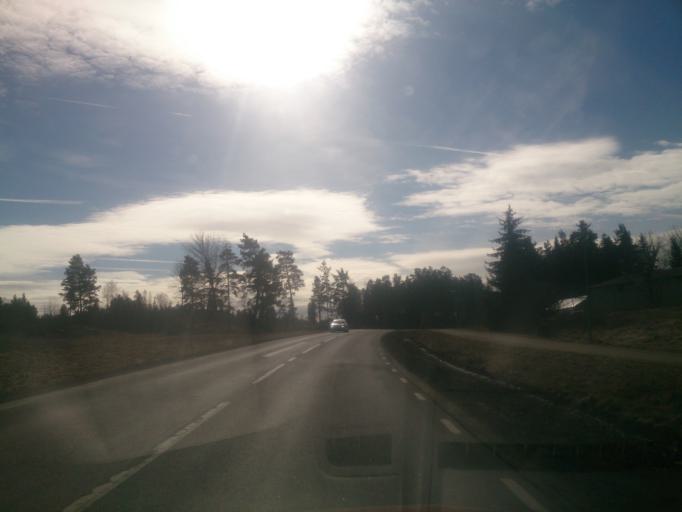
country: SE
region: OEstergoetland
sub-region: Finspangs Kommun
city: Finspang
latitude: 58.6929
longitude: 15.7511
